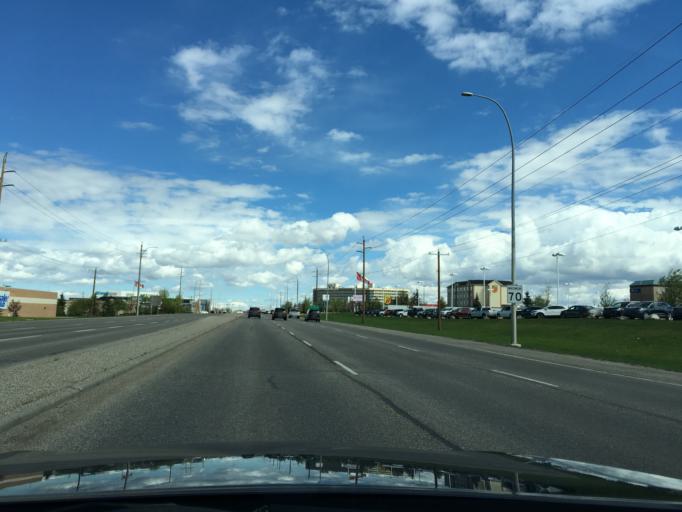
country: CA
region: Alberta
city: Calgary
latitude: 51.0775
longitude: -114.0016
